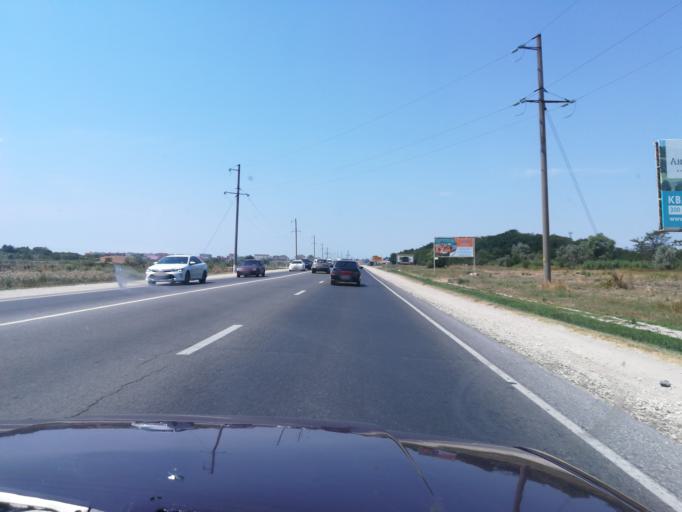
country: RU
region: Krasnodarskiy
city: Tsibanobalka
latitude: 44.9544
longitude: 37.3110
